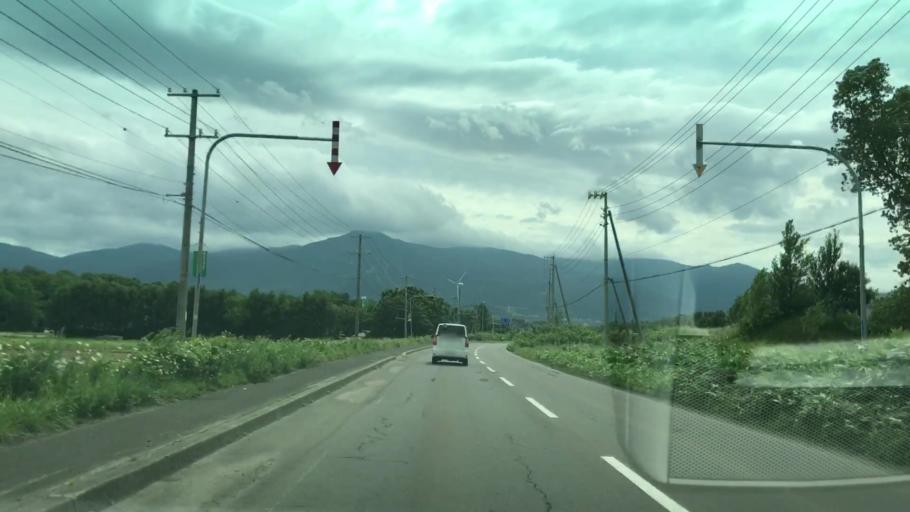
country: JP
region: Hokkaido
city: Iwanai
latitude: 43.0033
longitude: 140.5416
